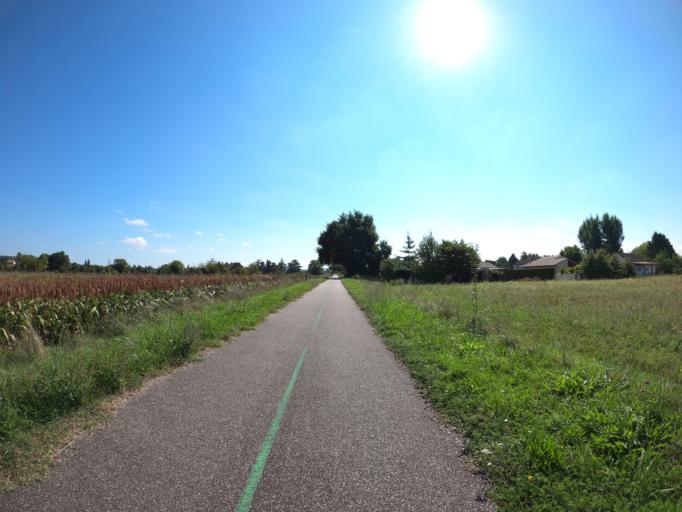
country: FR
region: Aquitaine
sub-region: Departement du Lot-et-Garonne
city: Casseneuil
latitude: 44.4335
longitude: 0.6378
